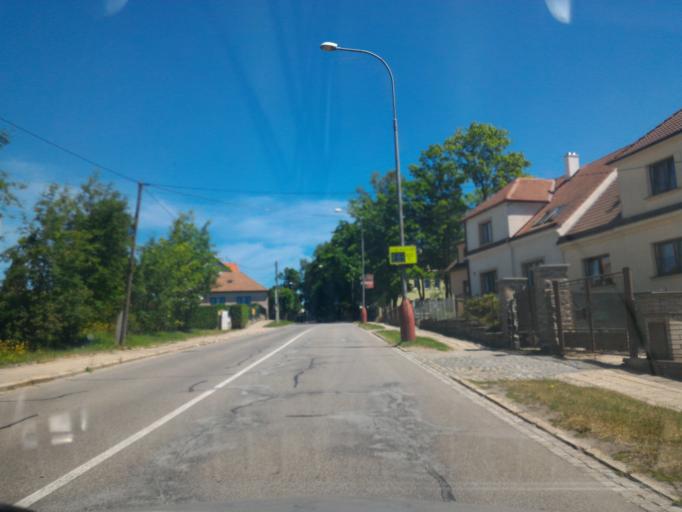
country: CZ
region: Vysocina
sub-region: Okres Jihlava
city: Trest'
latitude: 49.2839
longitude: 15.4798
